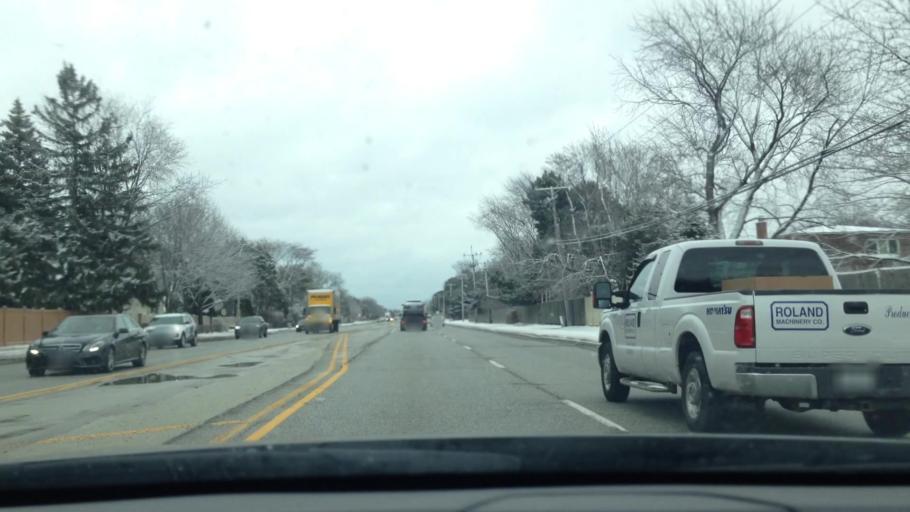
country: US
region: Illinois
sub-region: Cook County
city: Northbrook
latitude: 42.1056
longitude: -87.8377
